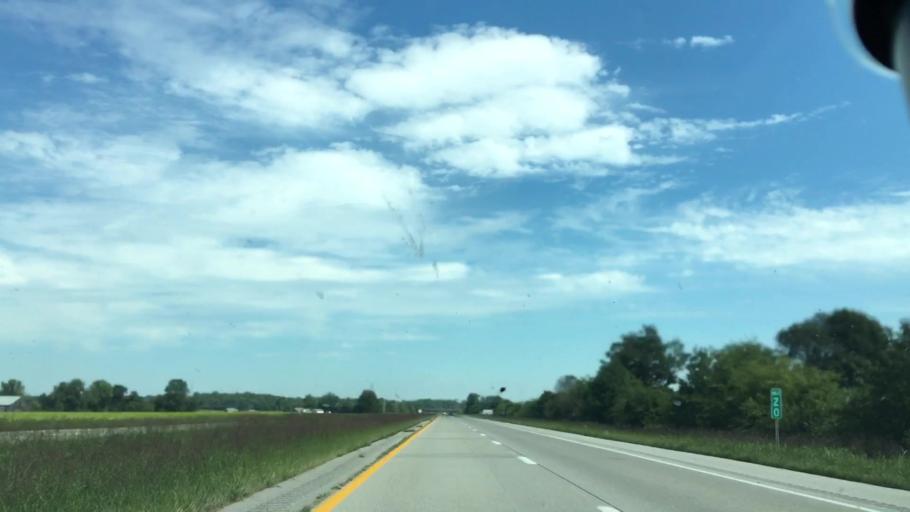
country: US
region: Kentucky
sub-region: Daviess County
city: Owensboro
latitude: 37.7624
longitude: -87.2253
